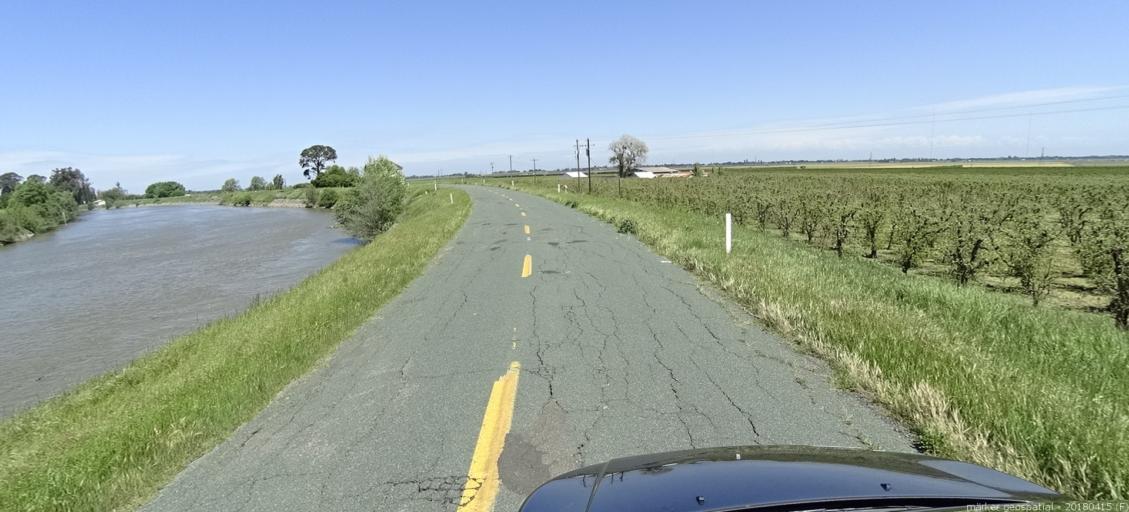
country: US
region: California
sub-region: Sacramento County
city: Walnut Grove
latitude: 38.2623
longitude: -121.5883
